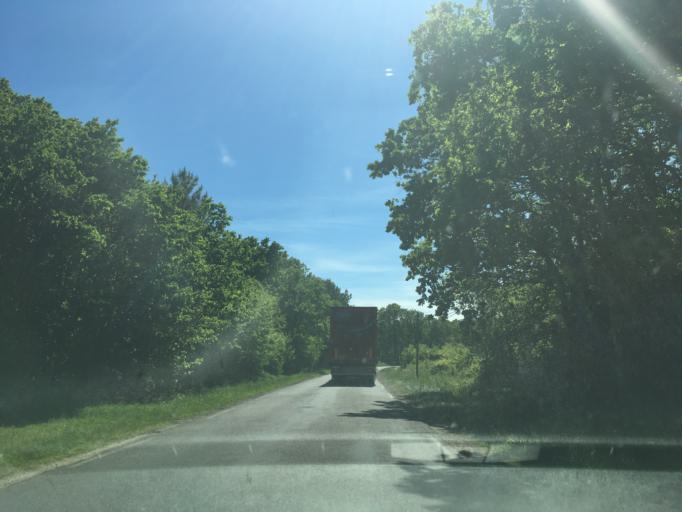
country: FR
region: Aquitaine
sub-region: Departement de la Gironde
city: Lesparre-Medoc
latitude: 45.2665
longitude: -0.8952
